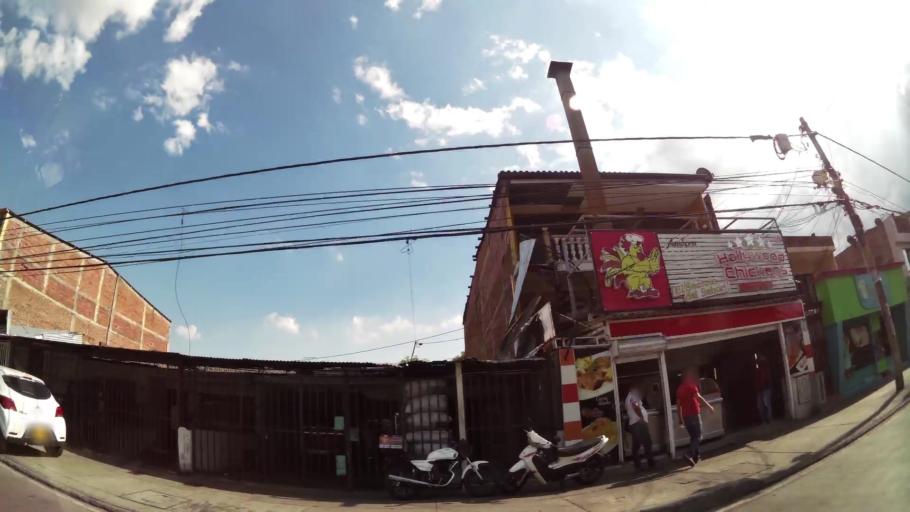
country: CO
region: Valle del Cauca
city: Cali
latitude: 3.4194
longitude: -76.5167
